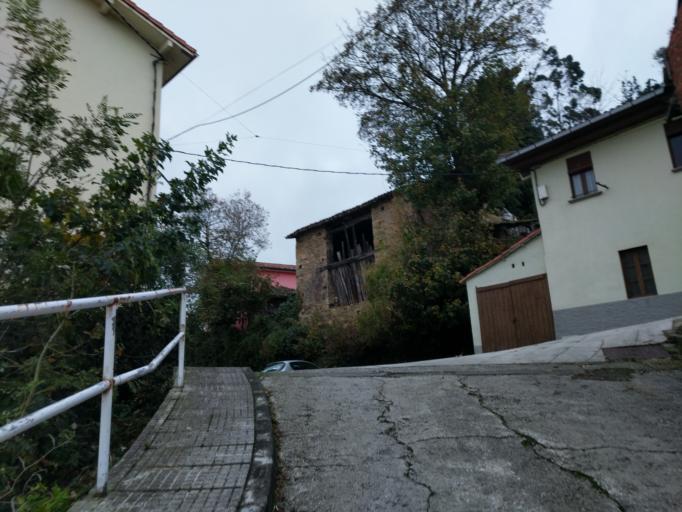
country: ES
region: Asturias
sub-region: Province of Asturias
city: Tineo
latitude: 43.3360
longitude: -6.4124
